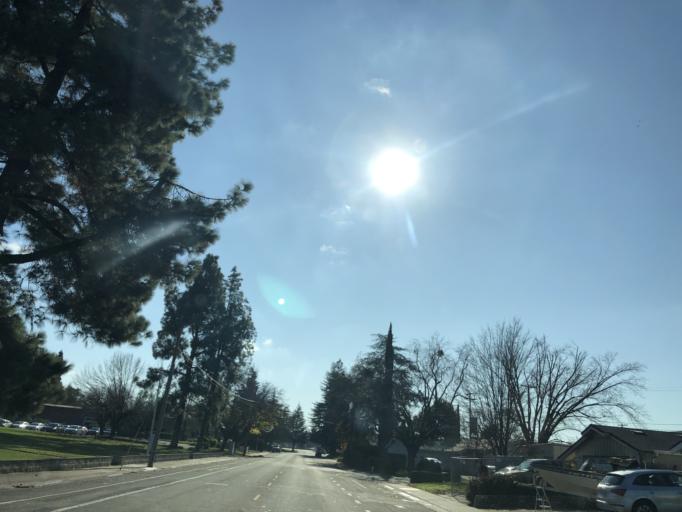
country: US
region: California
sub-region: Sacramento County
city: Rosemont
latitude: 38.5531
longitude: -121.3817
